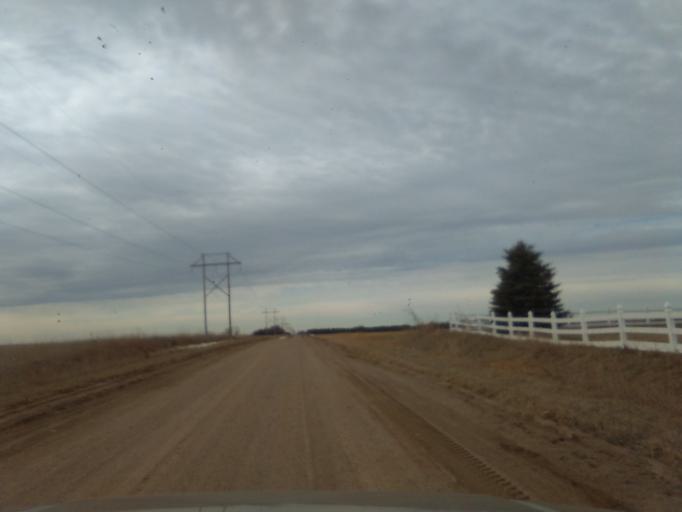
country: US
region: Nebraska
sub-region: Buffalo County
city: Gibbon
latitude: 40.6549
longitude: -98.7638
